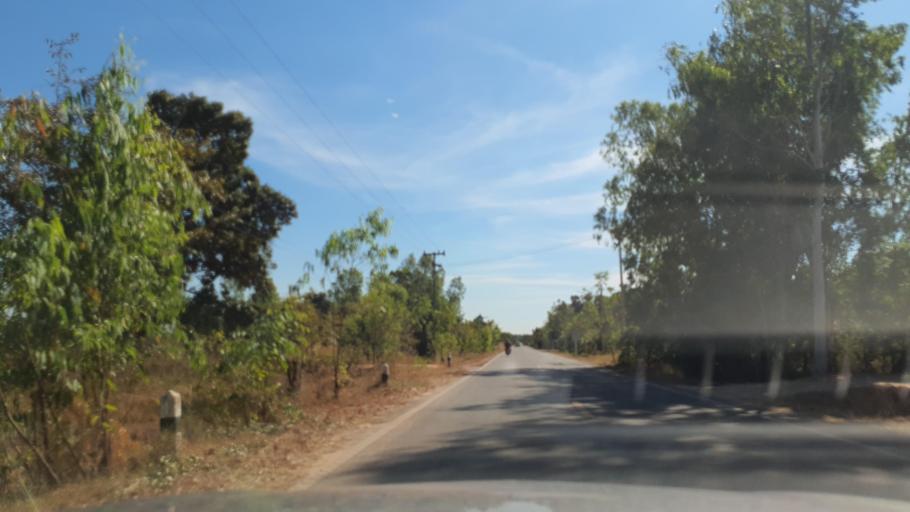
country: TH
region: Kalasin
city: Khao Wong
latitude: 16.7100
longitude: 104.1146
